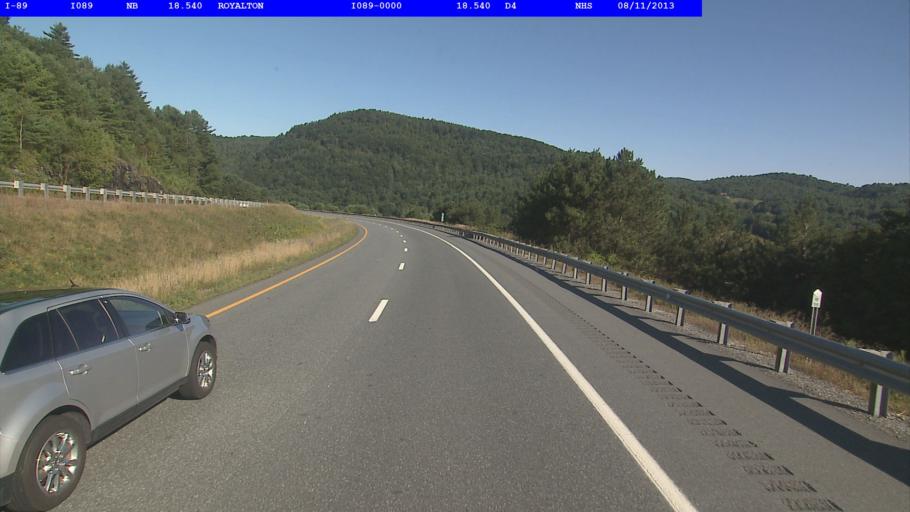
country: US
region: Vermont
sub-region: Orange County
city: Randolph
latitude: 43.8210
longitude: -72.5272
